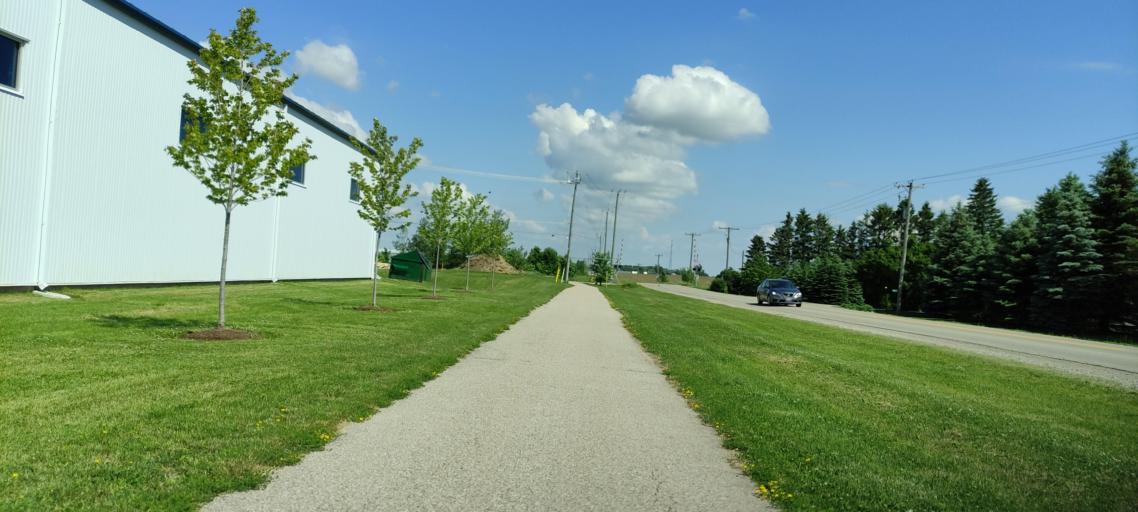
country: CA
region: Ontario
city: Stratford
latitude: 43.3456
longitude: -81.0210
